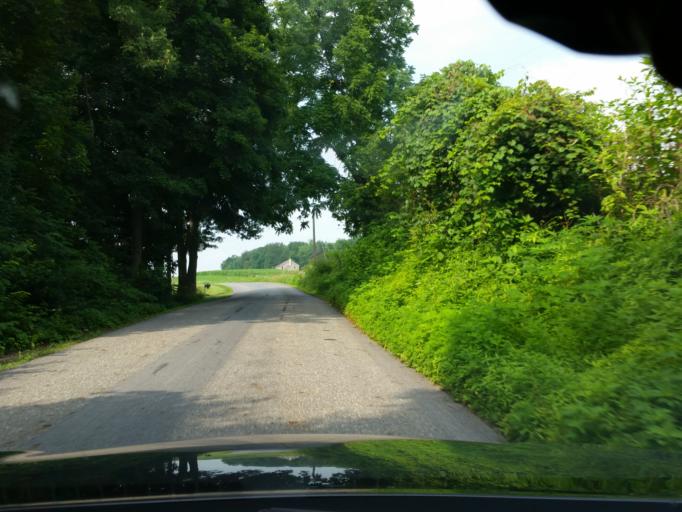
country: US
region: Pennsylvania
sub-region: Juniata County
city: Mifflintown
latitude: 40.3777
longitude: -77.4128
